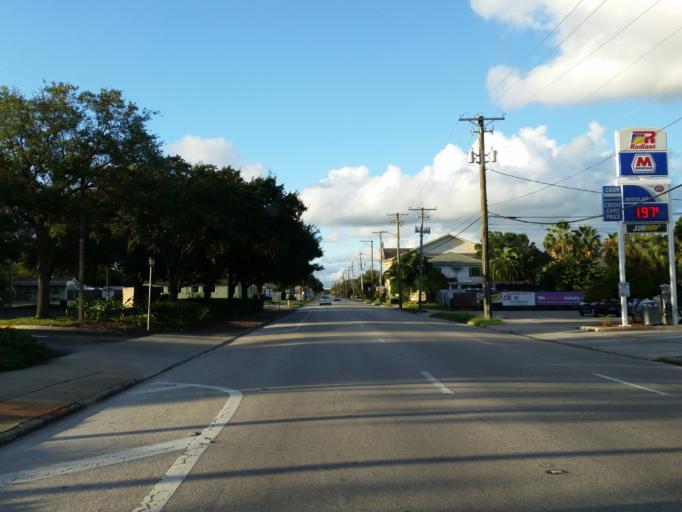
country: US
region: Florida
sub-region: Hillsborough County
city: Tampa
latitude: 27.9450
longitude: -82.4830
